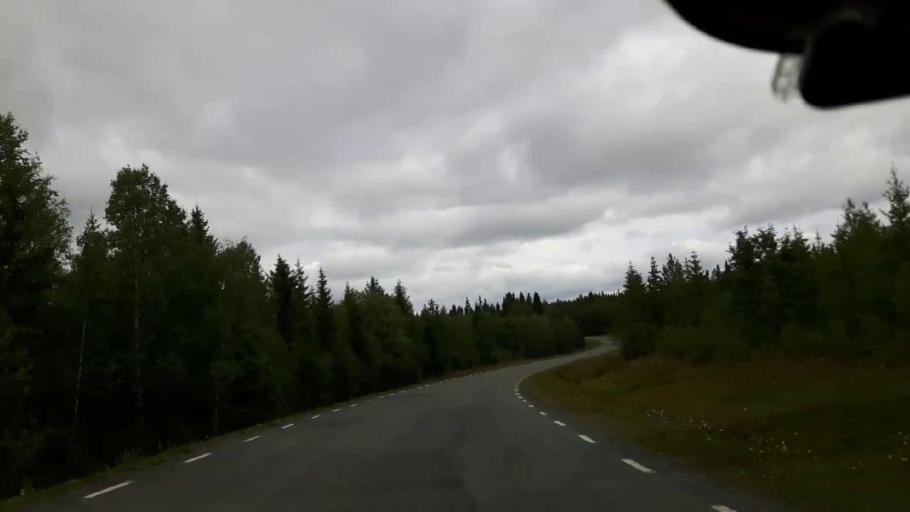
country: SE
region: Jaemtland
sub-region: Krokoms Kommun
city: Valla
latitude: 63.5287
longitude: 13.8710
